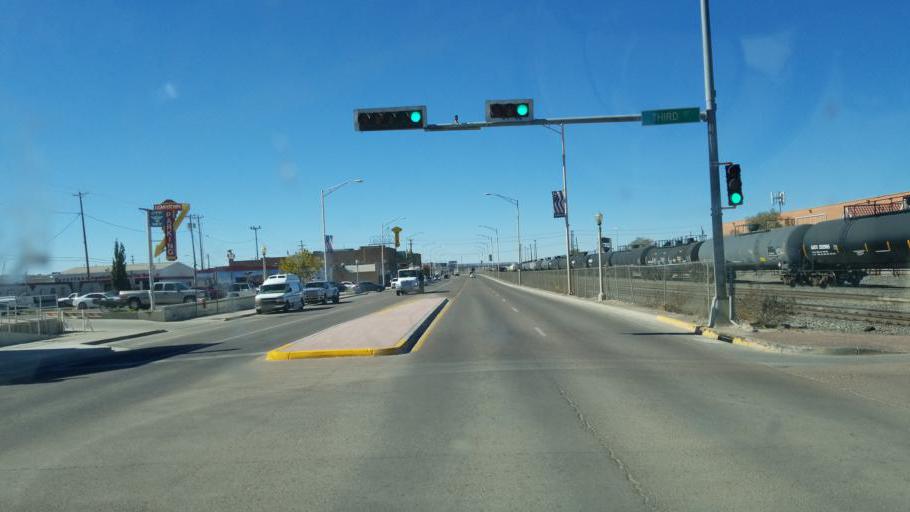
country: US
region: New Mexico
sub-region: McKinley County
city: Gallup
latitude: 35.5276
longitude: -108.7444
